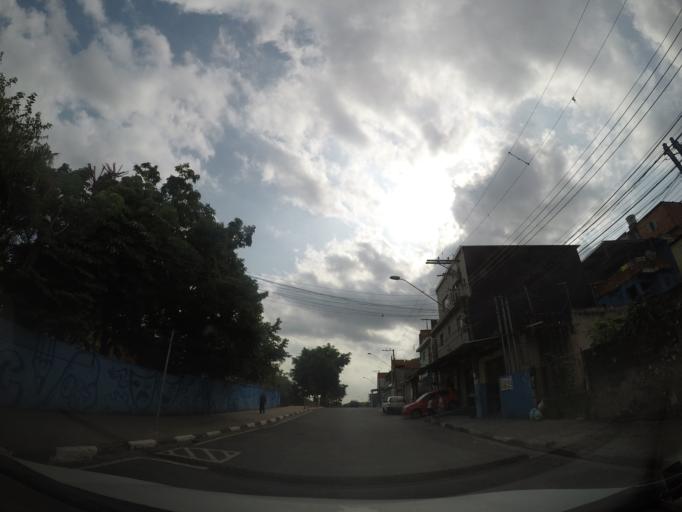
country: BR
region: Sao Paulo
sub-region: Guarulhos
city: Guarulhos
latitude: -23.4044
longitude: -46.4533
